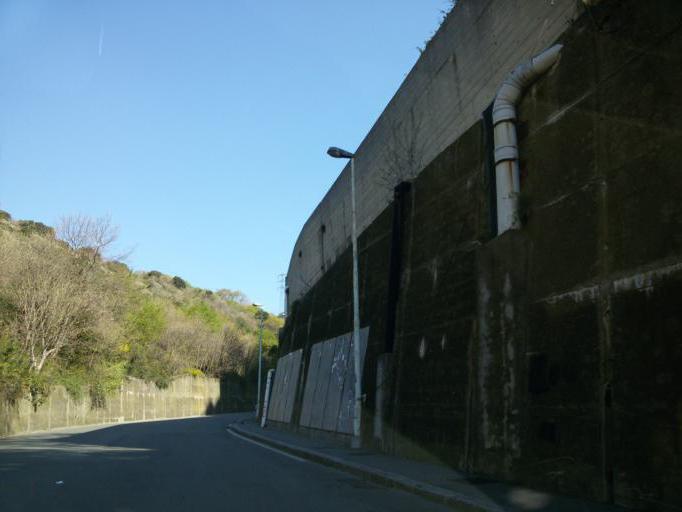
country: IT
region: Liguria
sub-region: Provincia di Genova
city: Genoa
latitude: 44.4223
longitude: 8.9086
